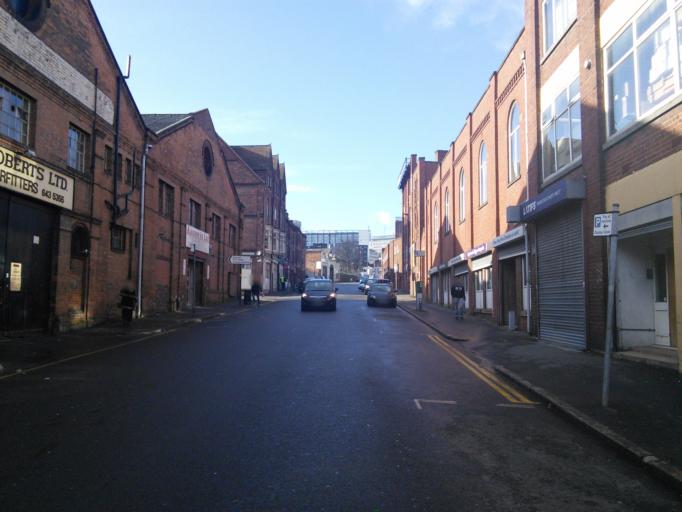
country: GB
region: England
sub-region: City and Borough of Birmingham
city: Birmingham
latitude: 52.4785
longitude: -1.8887
